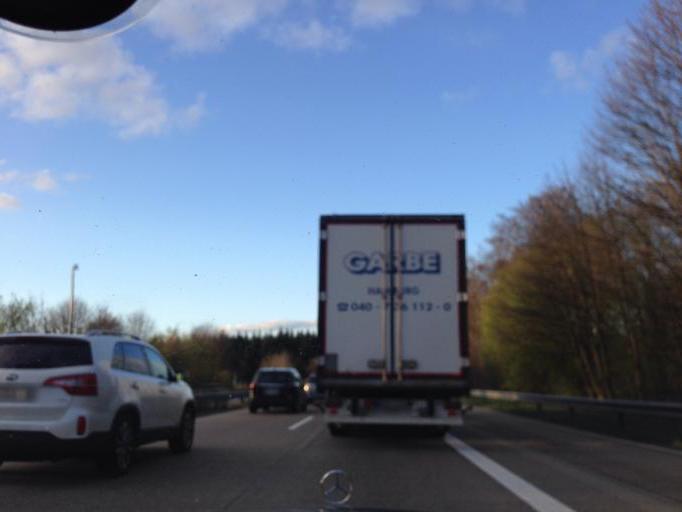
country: DE
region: Lower Saxony
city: Bad Fallingbostel
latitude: 52.8400
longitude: 9.6872
